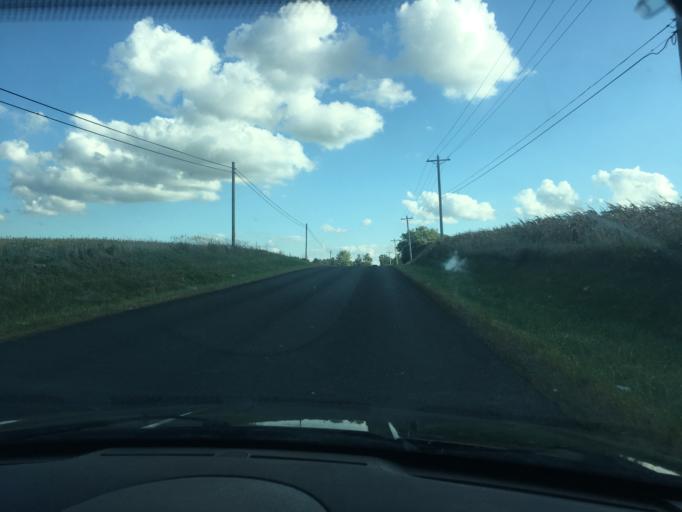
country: US
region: Ohio
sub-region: Logan County
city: Bellefontaine
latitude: 40.3218
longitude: -83.7398
